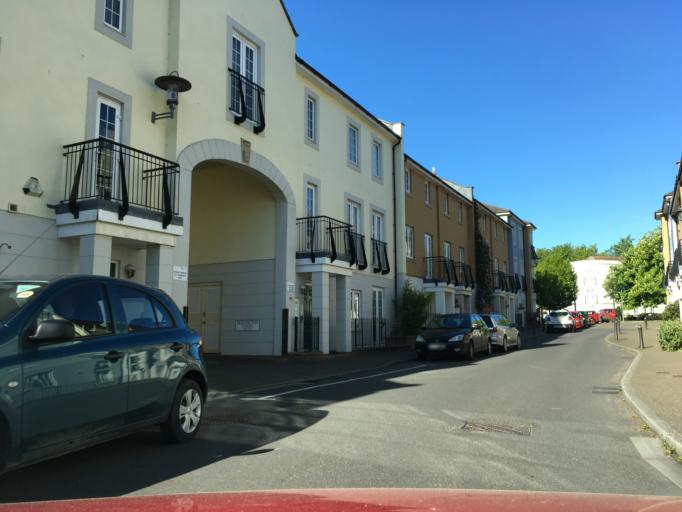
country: GB
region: England
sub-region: North Somerset
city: Portishead
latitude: 51.4893
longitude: -2.7622
